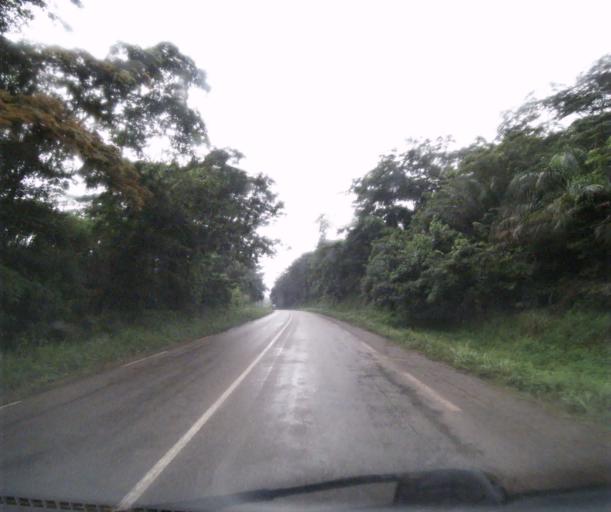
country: CM
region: Centre
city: Eseka
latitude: 3.8731
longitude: 10.6297
